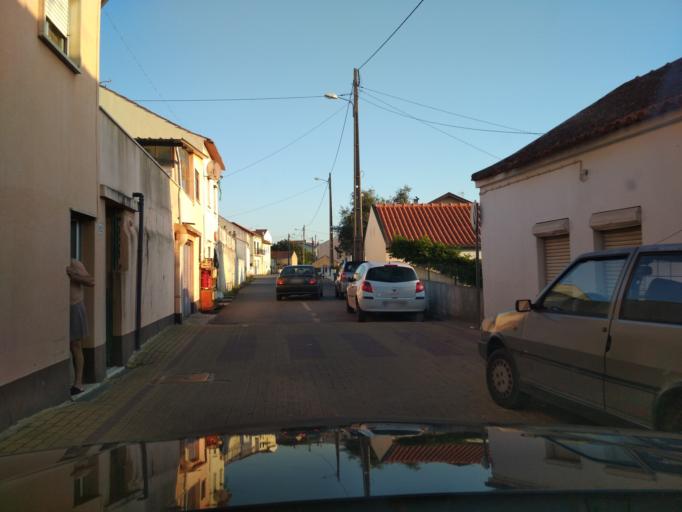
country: PT
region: Coimbra
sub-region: Coimbra
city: Coimbra
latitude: 40.2377
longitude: -8.4086
